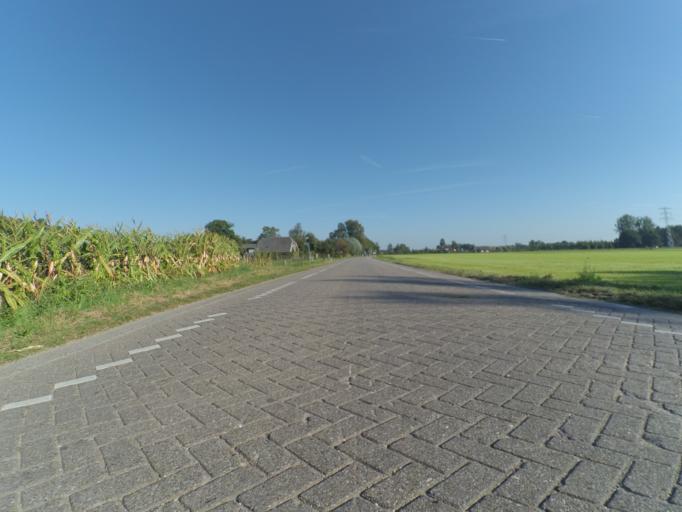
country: NL
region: Gelderland
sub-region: Gemeente Ermelo
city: Horst
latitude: 52.2806
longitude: 5.5625
